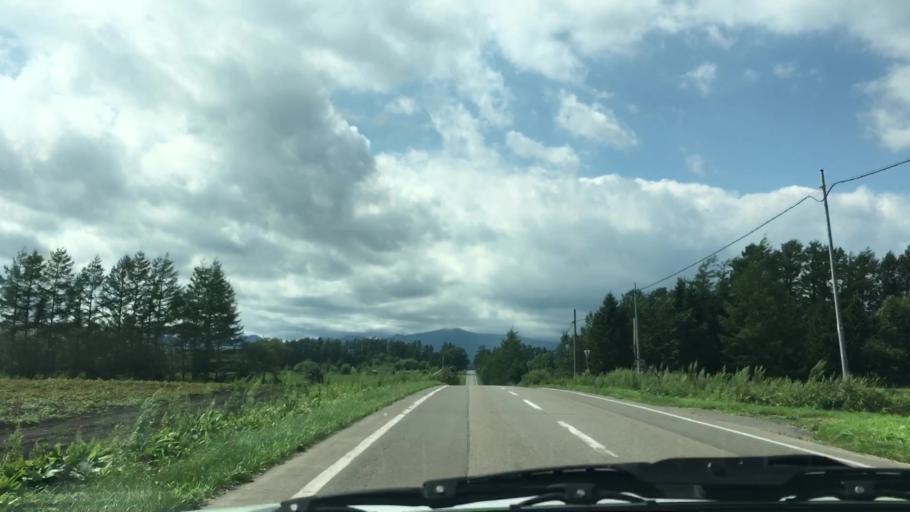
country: JP
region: Hokkaido
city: Otofuke
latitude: 43.2776
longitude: 143.3620
